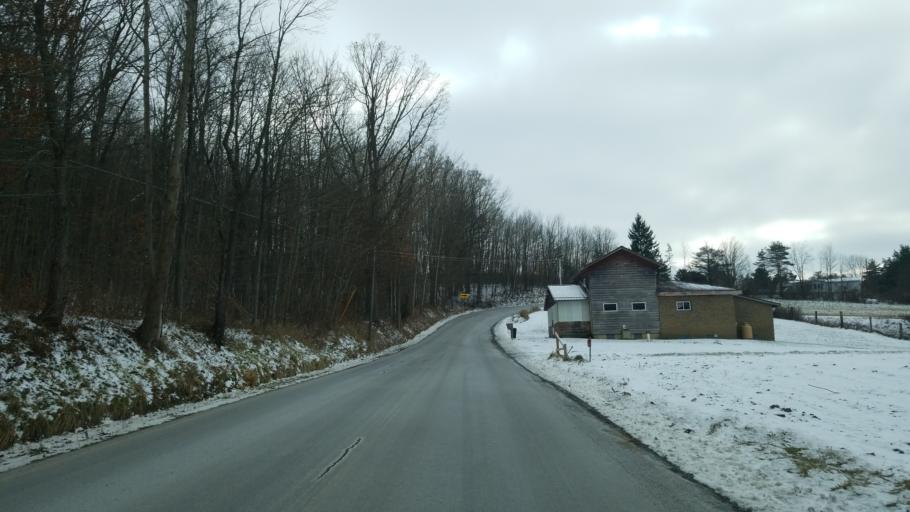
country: US
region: Pennsylvania
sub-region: Clearfield County
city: Sandy
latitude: 41.0894
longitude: -78.7490
